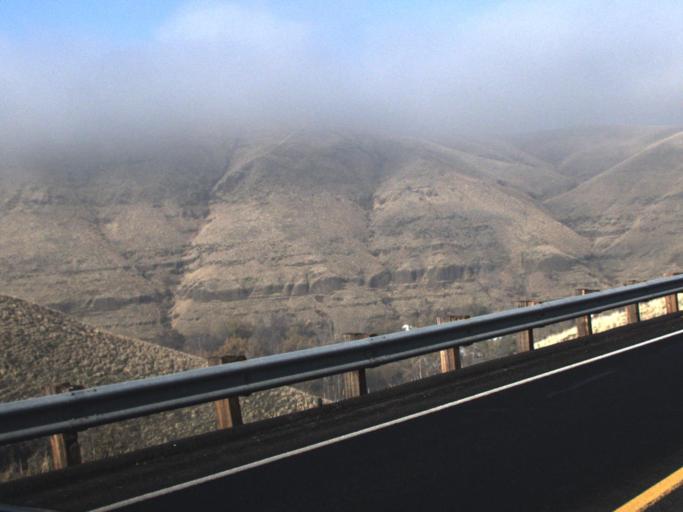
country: US
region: Washington
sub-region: Asotin County
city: Asotin
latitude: 46.3319
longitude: -117.0595
